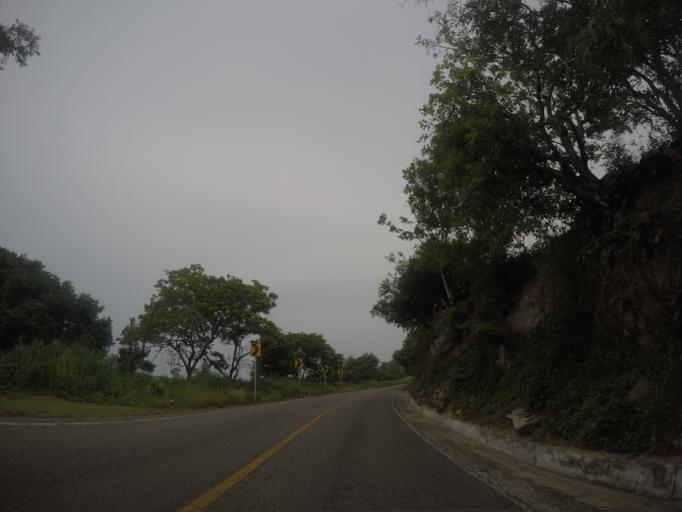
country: MX
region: Oaxaca
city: San Pedro Mixtepec
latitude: 15.9553
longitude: -97.2086
